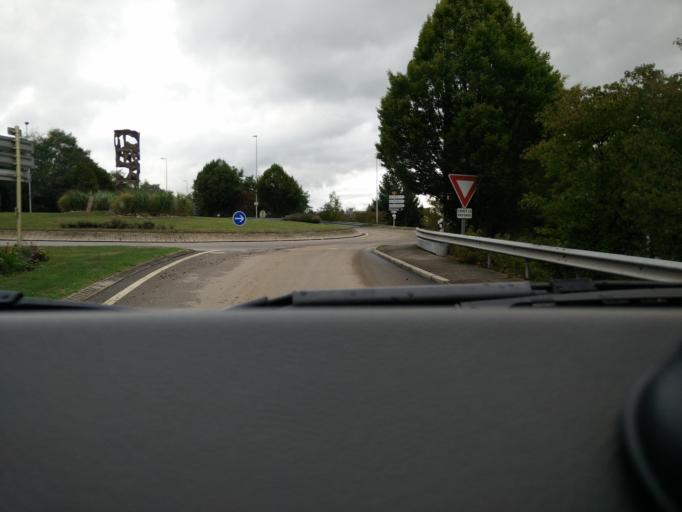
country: FR
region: Lorraine
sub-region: Departement des Vosges
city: Saint-Michel-sur-Meurthe
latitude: 48.3098
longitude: 6.9225
